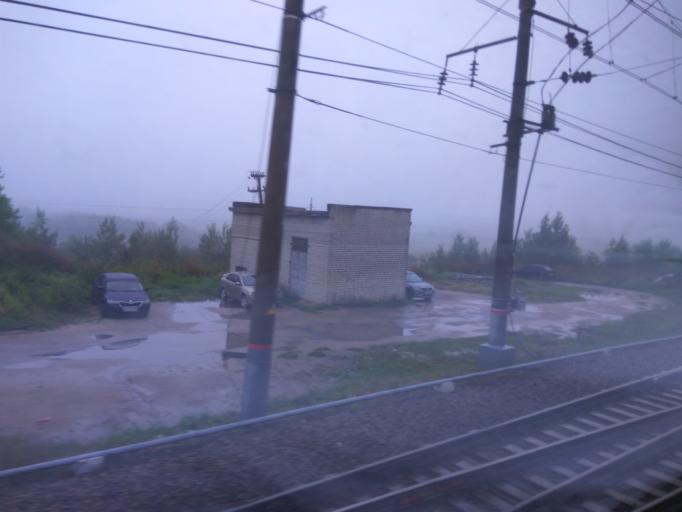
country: RU
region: Moskovskaya
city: Uzunovo
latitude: 54.5551
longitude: 38.6202
